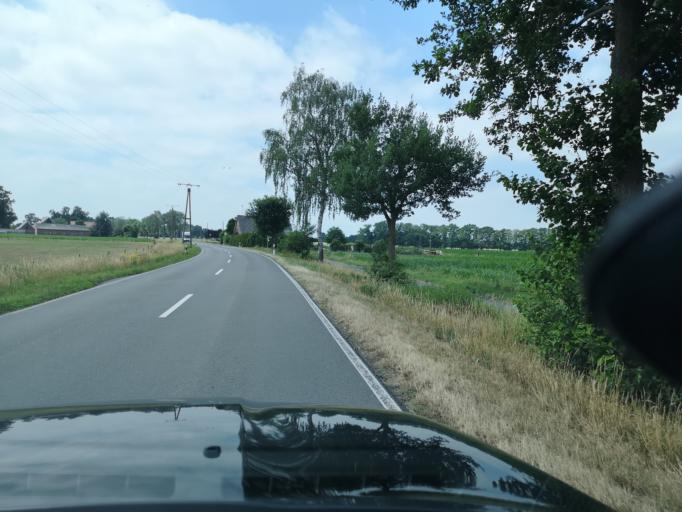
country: NL
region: Gelderland
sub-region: Gemeente Aalten
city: Aalten
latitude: 51.8751
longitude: 6.5657
